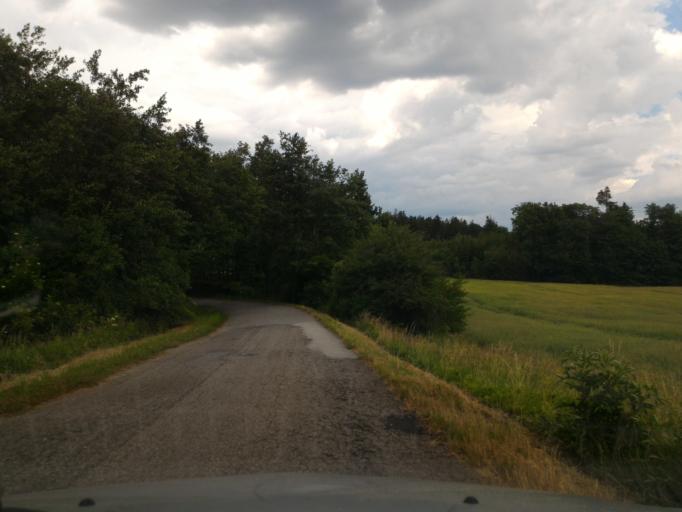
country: CZ
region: Vysocina
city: Zeletava
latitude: 49.0918
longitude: 15.6866
